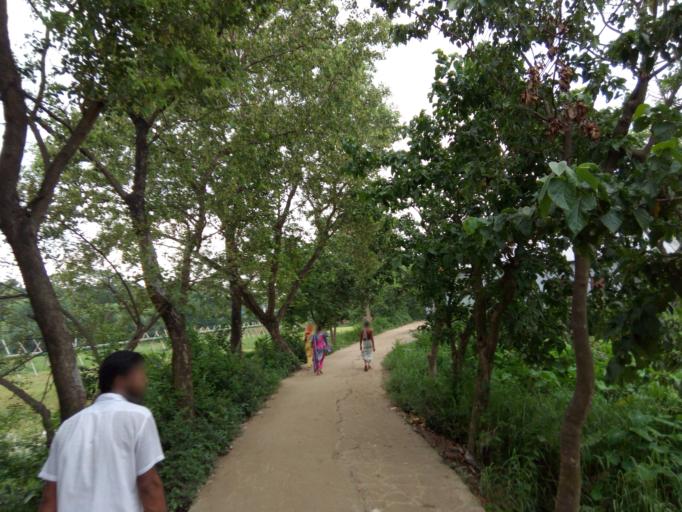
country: BD
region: Dhaka
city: Paltan
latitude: 23.7565
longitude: 90.4557
